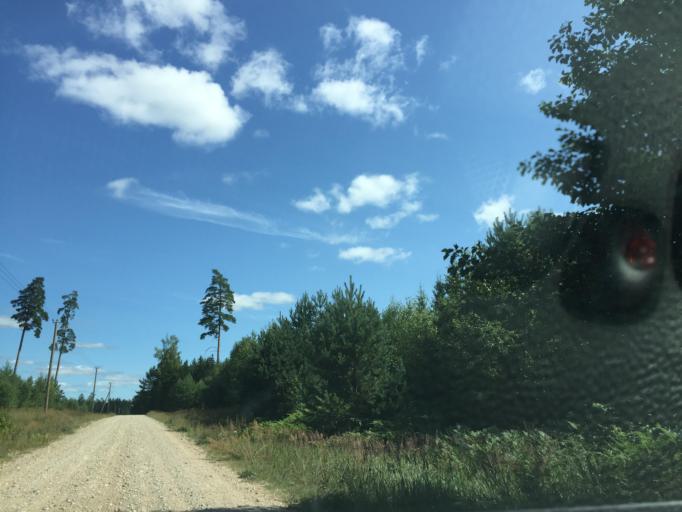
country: LV
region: Talsu Rajons
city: Stende
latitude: 57.1762
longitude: 22.3094
